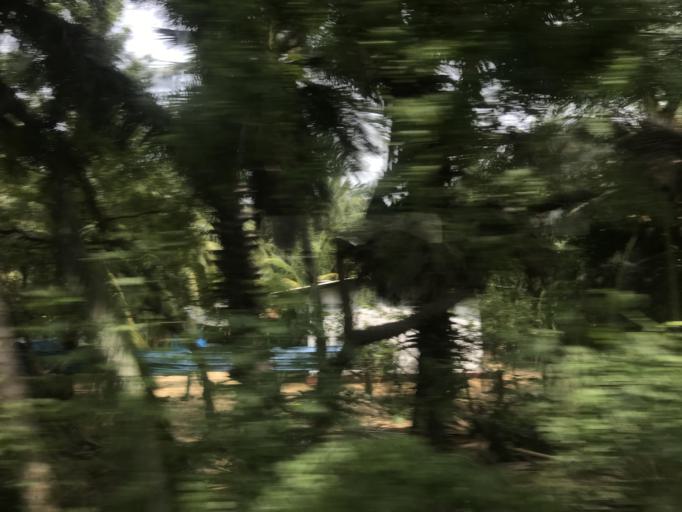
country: LK
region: Northern Province
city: Kilinochchi
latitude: 9.5980
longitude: 80.3407
